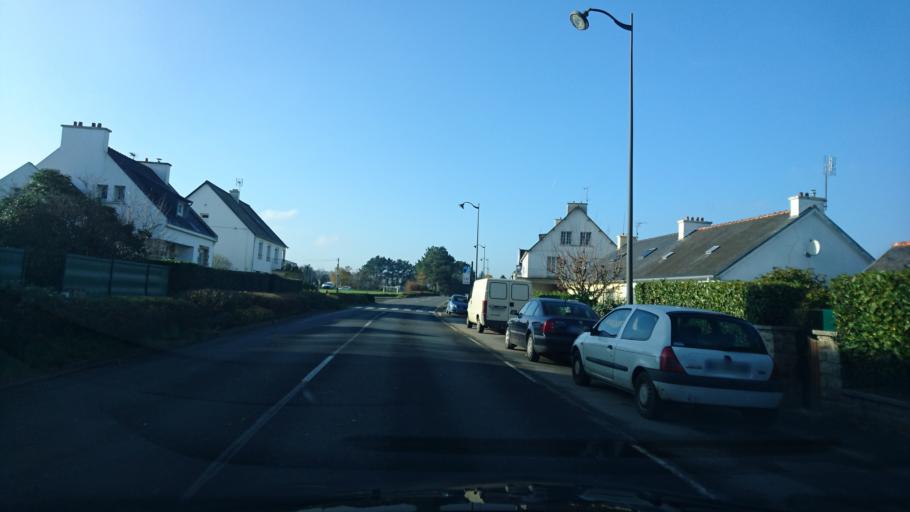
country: FR
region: Brittany
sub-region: Departement du Finistere
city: Le Faou
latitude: 48.2928
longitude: -4.1813
